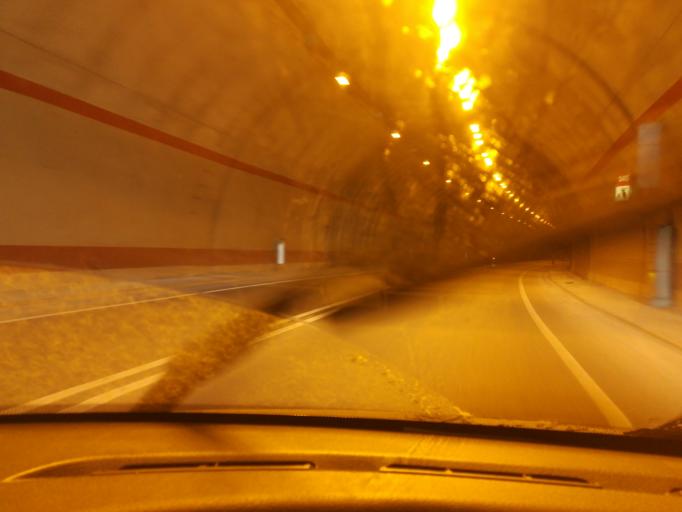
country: IT
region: The Marches
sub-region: Provincia di Macerata
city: Macerata
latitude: 43.2972
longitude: 13.4415
